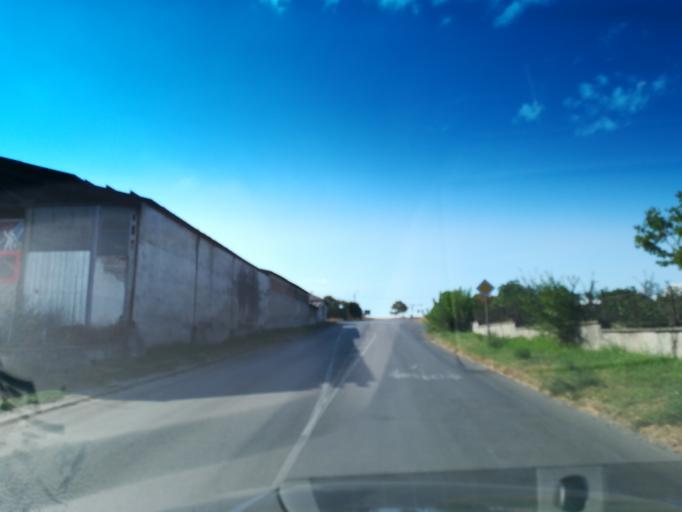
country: BG
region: Khaskovo
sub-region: Obshtina Mineralni Bani
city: Mineralni Bani
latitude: 42.0205
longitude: 25.4140
